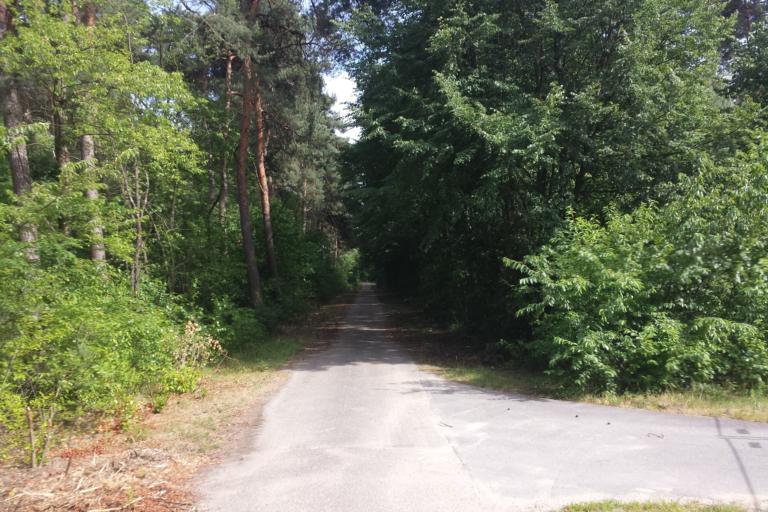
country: DE
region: Hesse
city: Viernheim
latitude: 49.5503
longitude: 8.5235
